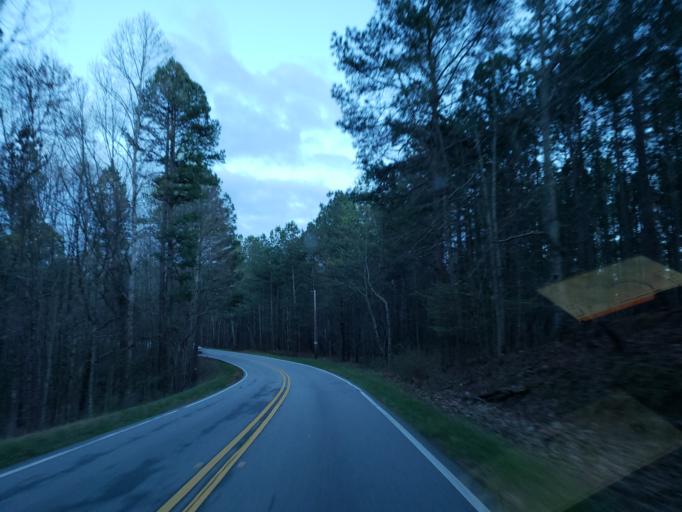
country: US
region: Georgia
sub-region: Polk County
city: Rockmart
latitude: 33.9912
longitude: -84.9305
